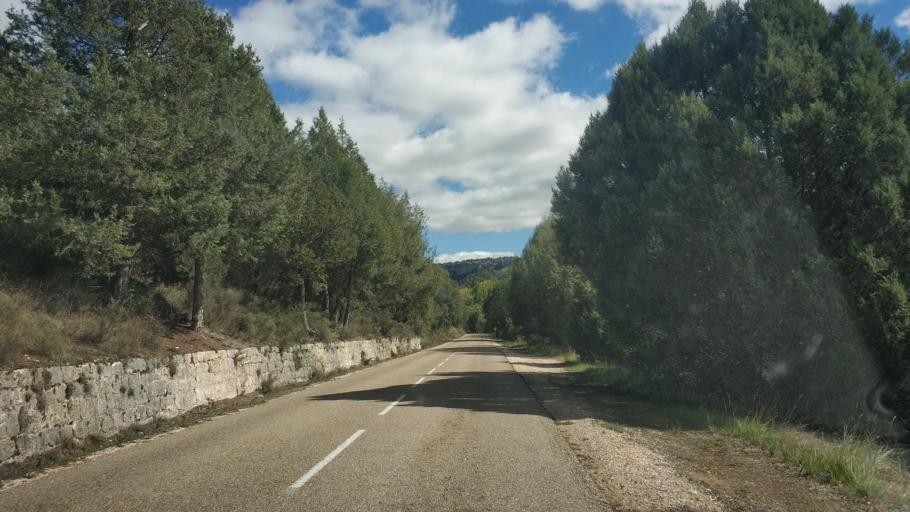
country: ES
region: Castille and Leon
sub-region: Provincia de Burgos
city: Hortiguela
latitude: 42.0485
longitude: -3.4646
